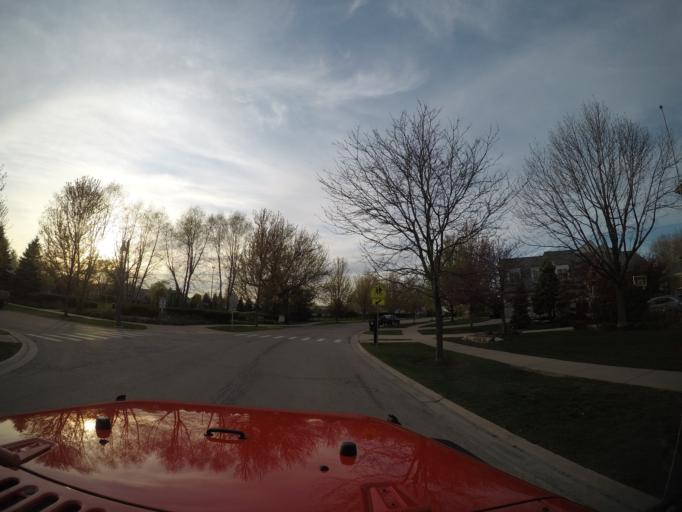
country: US
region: Illinois
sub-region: Cook County
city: Northbrook
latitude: 42.0864
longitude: -87.8341
